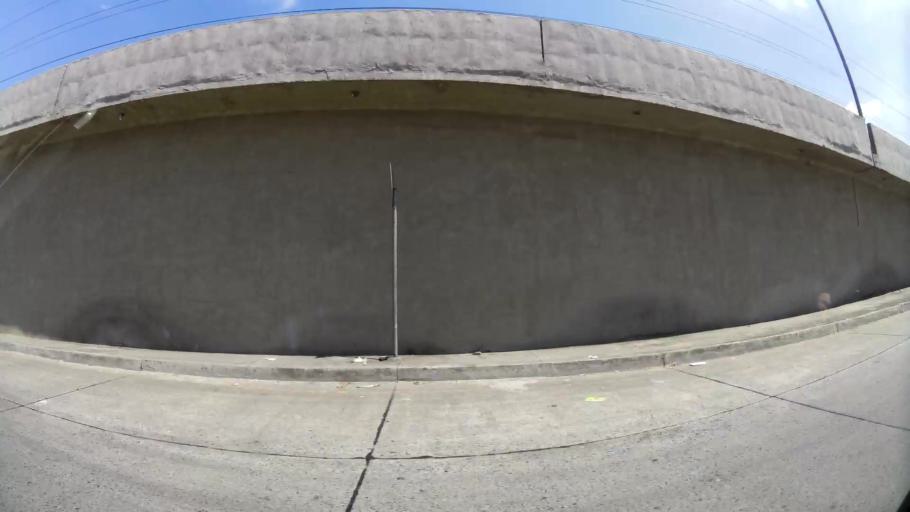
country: EC
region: Guayas
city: Eloy Alfaro
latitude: -2.1376
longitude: -79.9065
